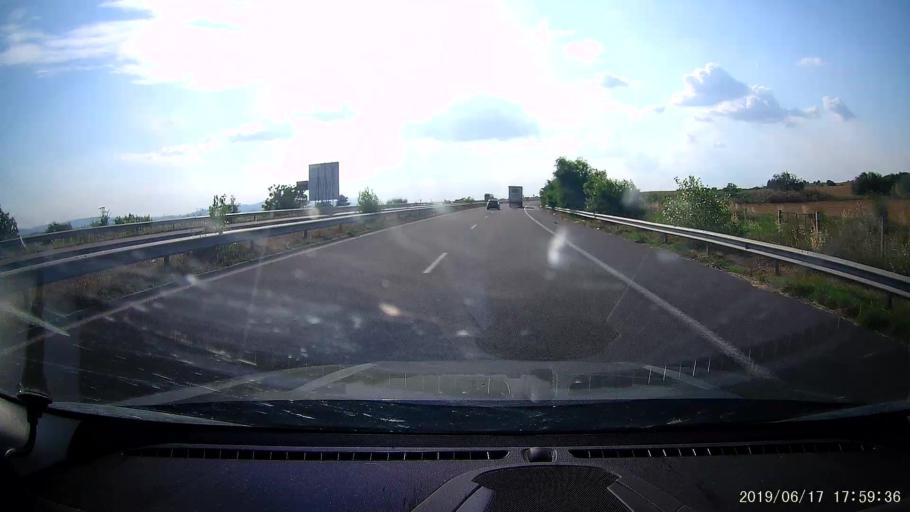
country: BG
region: Khaskovo
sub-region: Obshtina Svilengrad
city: Svilengrad
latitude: 41.7251
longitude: 26.2941
